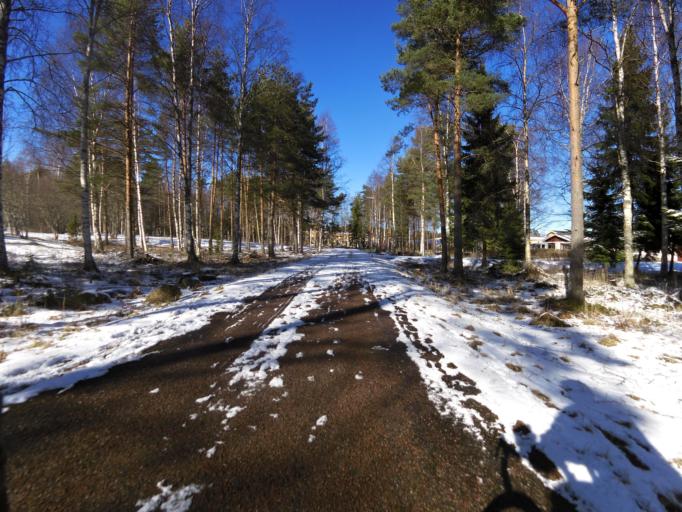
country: SE
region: Gaevleborg
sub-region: Gavle Kommun
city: Gavle
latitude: 60.6626
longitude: 17.2375
